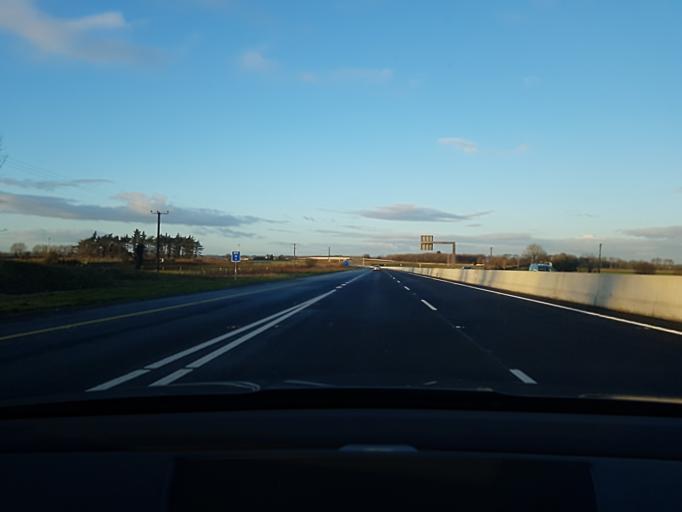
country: IE
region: Connaught
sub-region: County Galway
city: Athenry
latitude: 53.3053
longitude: -8.8021
